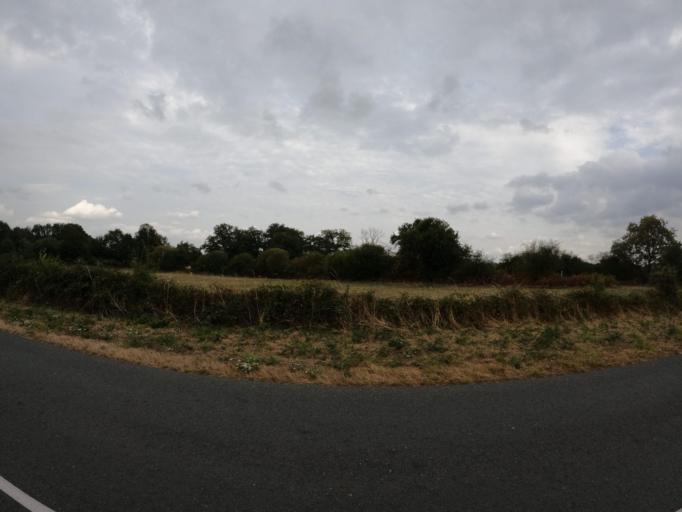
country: FR
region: Pays de la Loire
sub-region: Departement de Maine-et-Loire
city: Le Longeron
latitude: 47.0347
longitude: -1.0396
